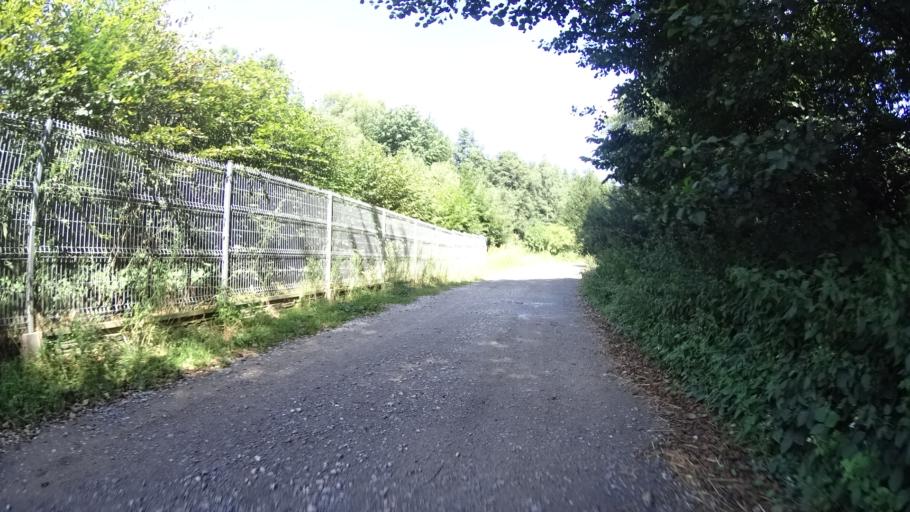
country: PL
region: Masovian Voivodeship
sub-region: Powiat grojecki
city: Mogielnica
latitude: 51.6710
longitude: 20.7453
